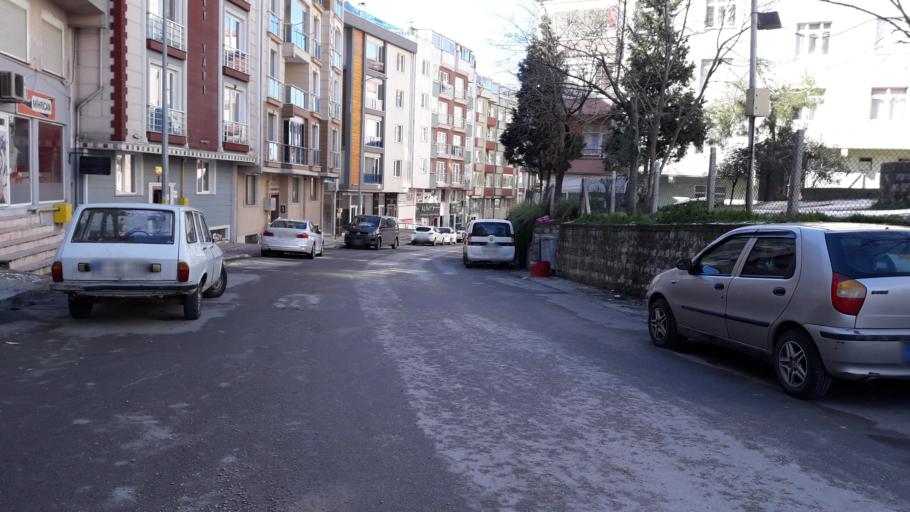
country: TR
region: Sinop
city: Sinop
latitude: 42.0227
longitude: 35.1593
